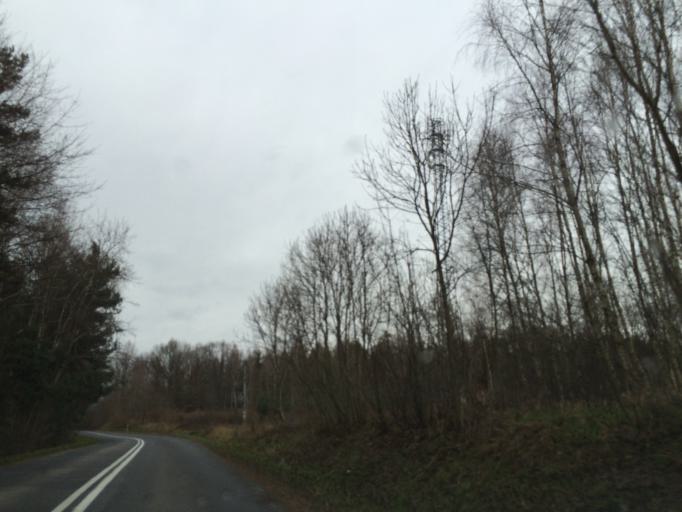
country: PL
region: Lower Silesian Voivodeship
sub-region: Powiat lwowecki
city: Lwowek Slaski
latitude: 51.1710
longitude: 15.5659
